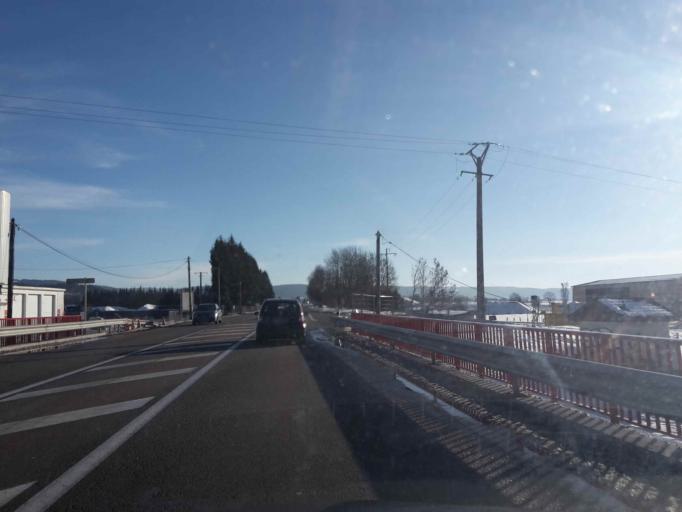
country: FR
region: Franche-Comte
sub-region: Departement du Doubs
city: Doubs
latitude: 46.9435
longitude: 6.3429
